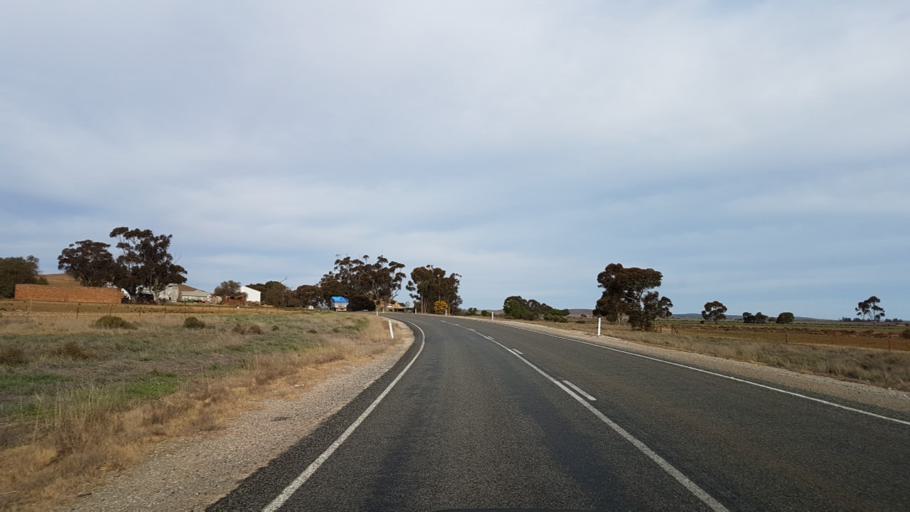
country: AU
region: South Australia
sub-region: Peterborough
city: Peterborough
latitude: -33.0269
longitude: 138.7252
